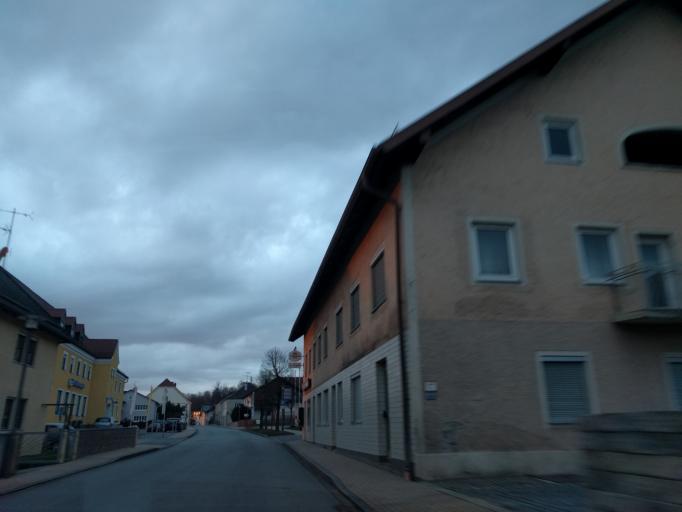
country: DE
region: Bavaria
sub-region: Lower Bavaria
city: Winzer
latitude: 48.7241
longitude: 13.0748
